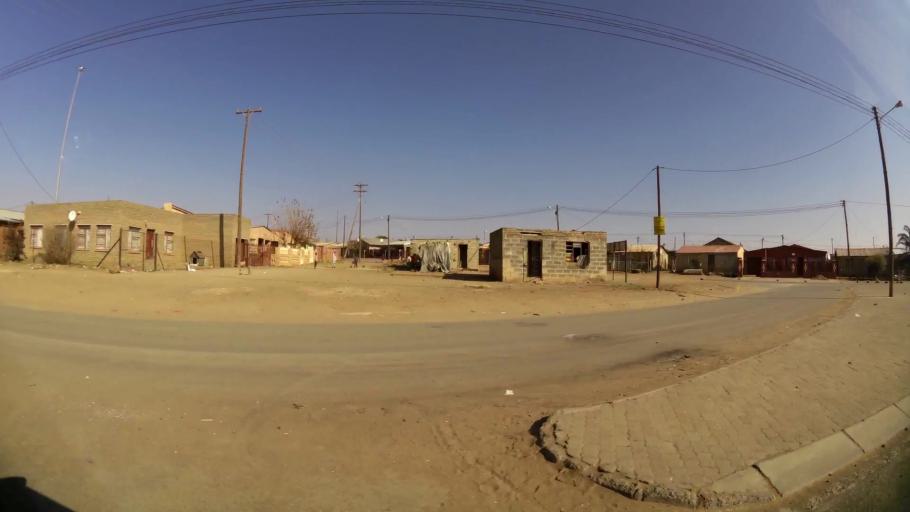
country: ZA
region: Orange Free State
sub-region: Mangaung Metropolitan Municipality
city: Bloemfontein
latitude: -29.1964
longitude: 26.2477
